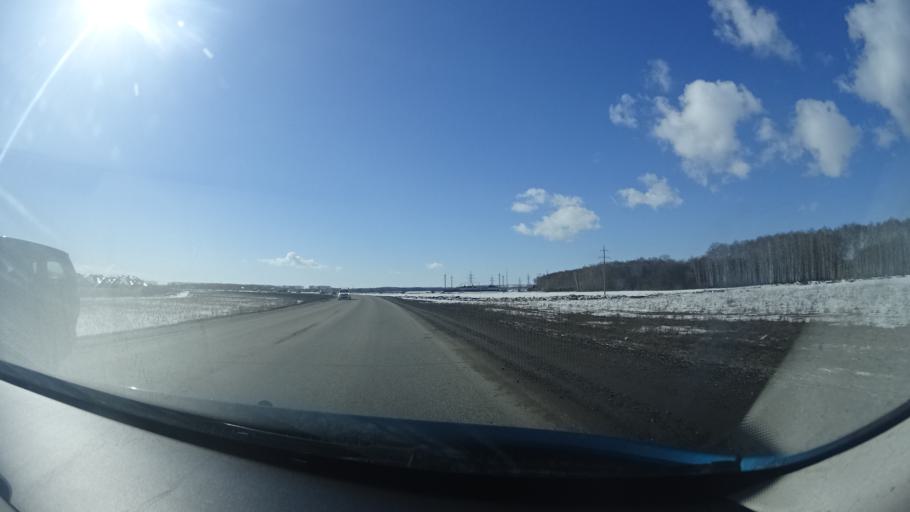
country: RU
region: Bashkortostan
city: Ufa
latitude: 54.6293
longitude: 55.8972
